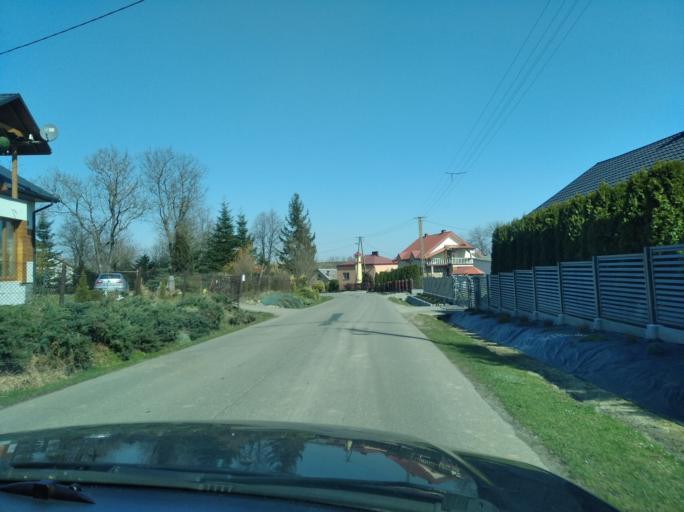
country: PL
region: Subcarpathian Voivodeship
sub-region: Powiat przeworski
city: Pantalowice
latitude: 49.9346
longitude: 22.4450
